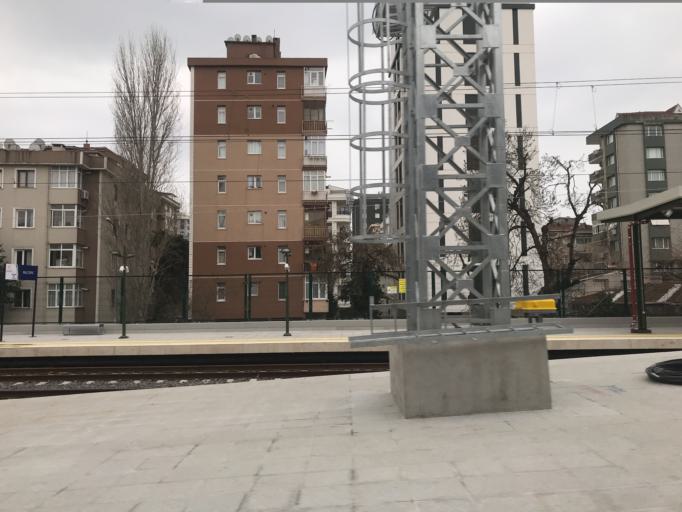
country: TR
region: Istanbul
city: Maltepe
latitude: 40.9201
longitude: 29.1348
